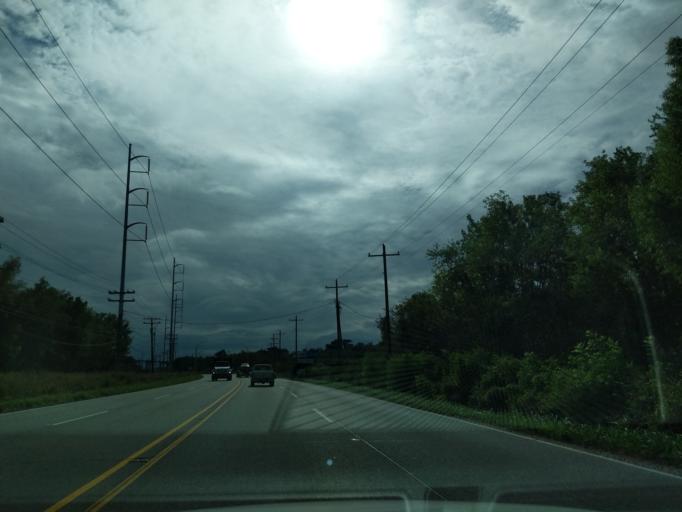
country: US
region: Louisiana
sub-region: Saint Bernard Parish
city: Chalmette
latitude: 30.0191
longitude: -89.9298
